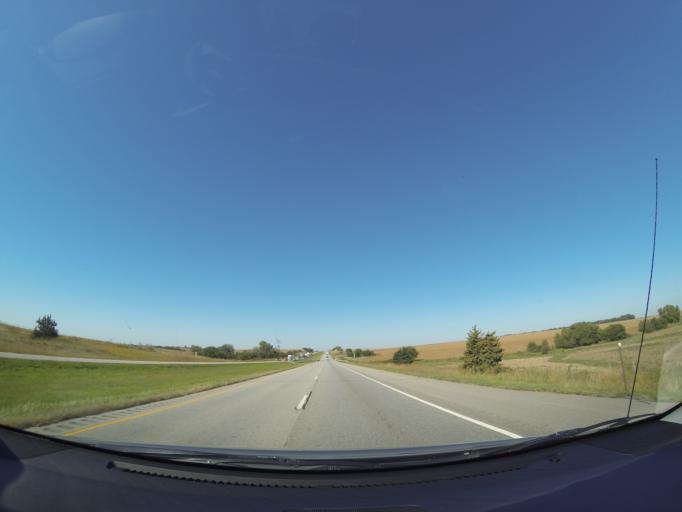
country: US
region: Nebraska
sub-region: Seward County
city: Seward
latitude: 40.8224
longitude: -97.1335
